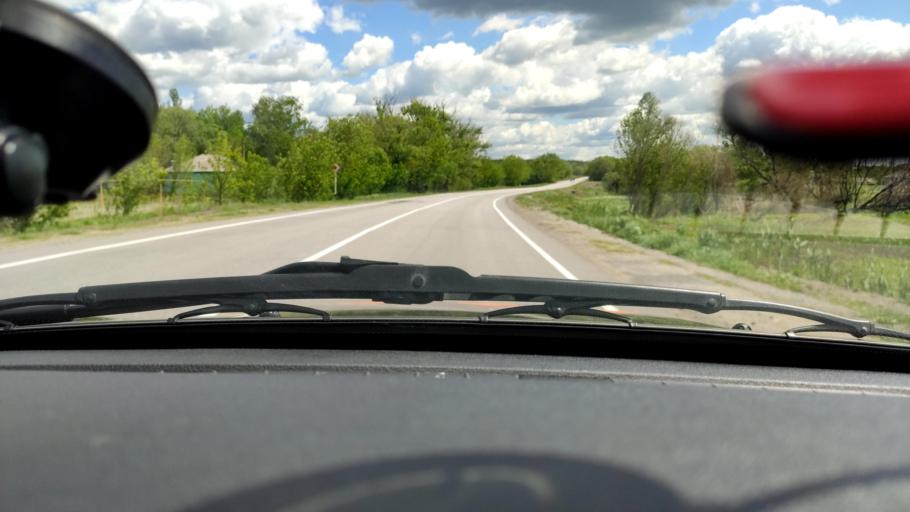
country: RU
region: Voronezj
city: Ostrogozhsk
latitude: 51.0554
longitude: 38.9205
